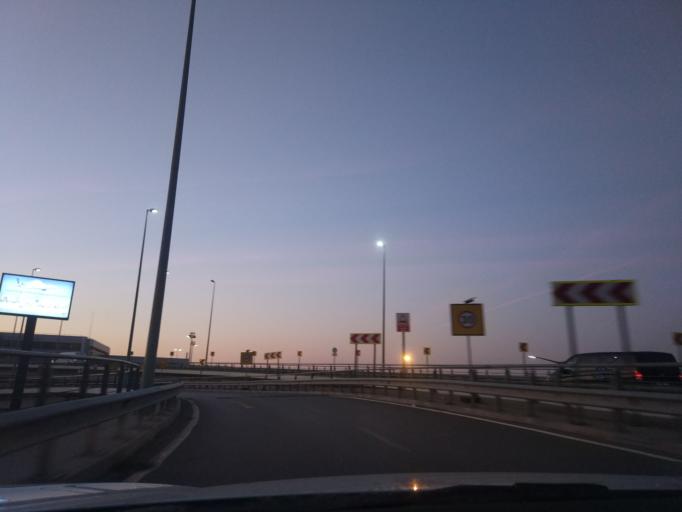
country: TR
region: Istanbul
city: Pendik
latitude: 40.9080
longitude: 29.3114
